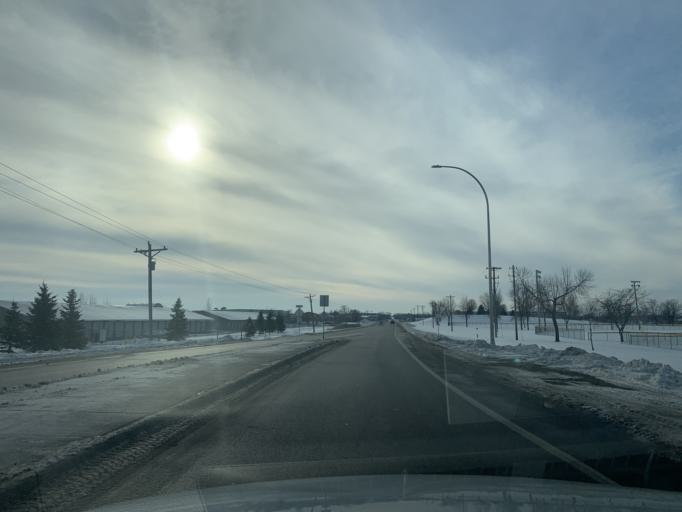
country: US
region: Minnesota
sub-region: Wright County
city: Buffalo
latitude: 45.1652
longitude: -93.8473
